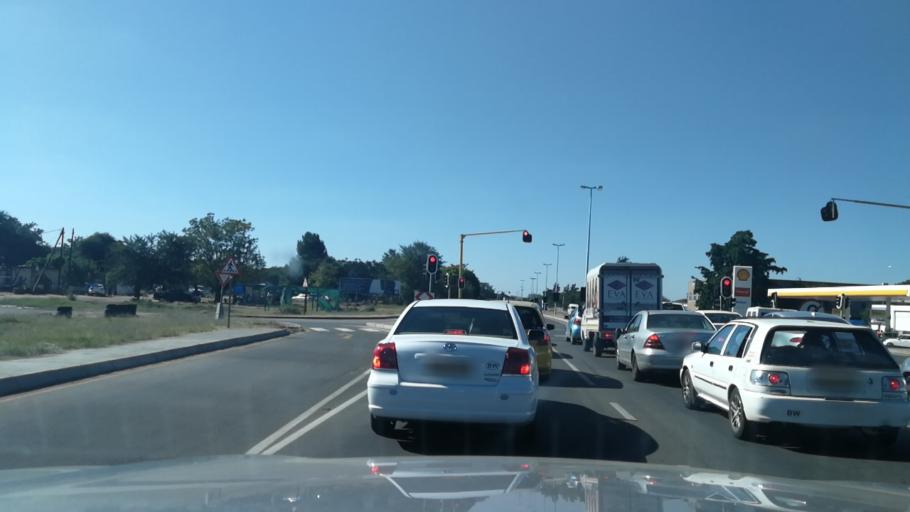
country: BW
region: South East
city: Gaborone
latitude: -24.6777
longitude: 25.9193
